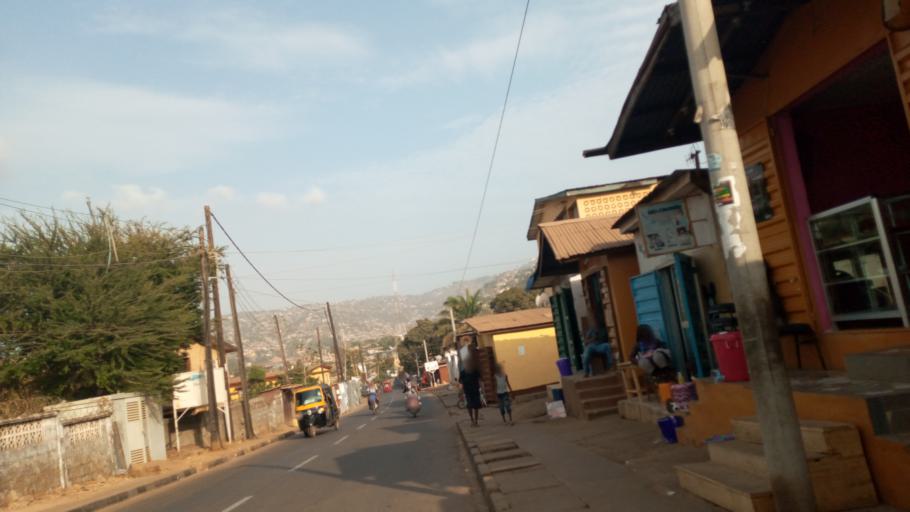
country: SL
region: Western Area
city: Freetown
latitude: 8.4747
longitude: -13.2543
